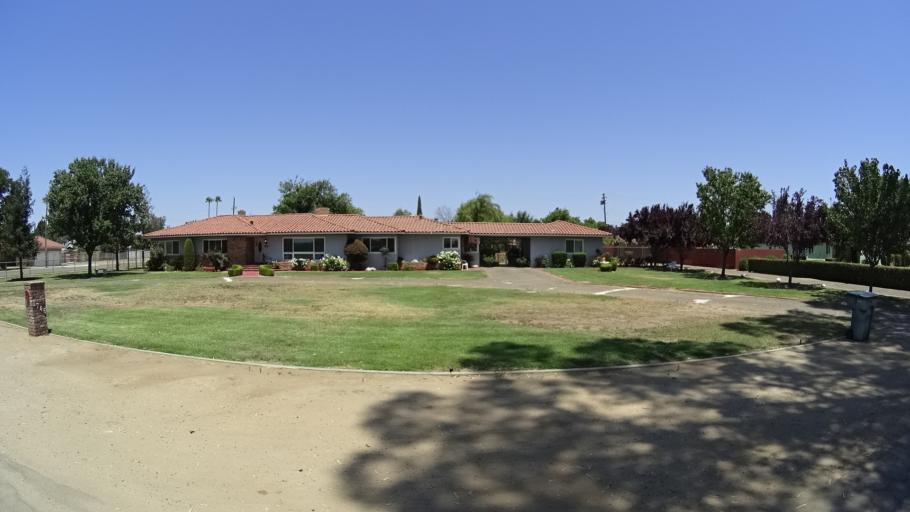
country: US
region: California
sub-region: Fresno County
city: West Park
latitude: 36.7286
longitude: -119.8318
